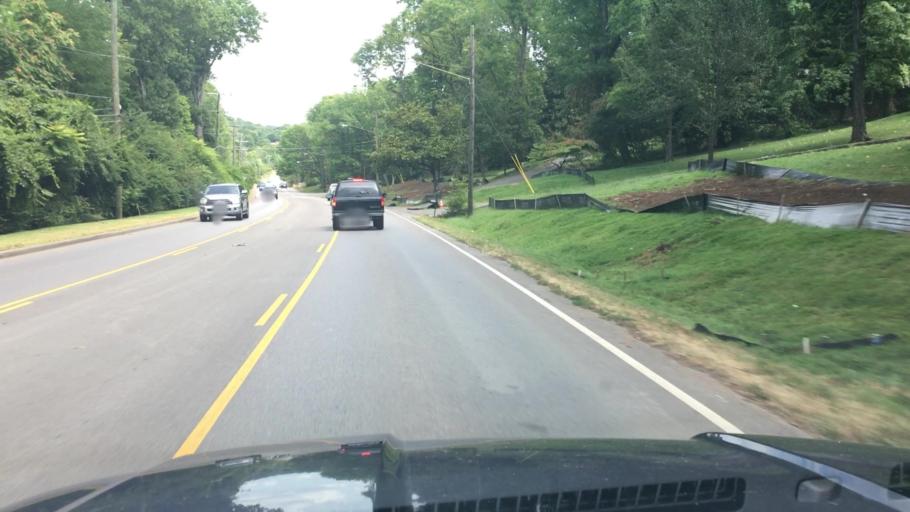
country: US
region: Tennessee
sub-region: Davidson County
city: Forest Hills
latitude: 36.0909
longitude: -86.8246
